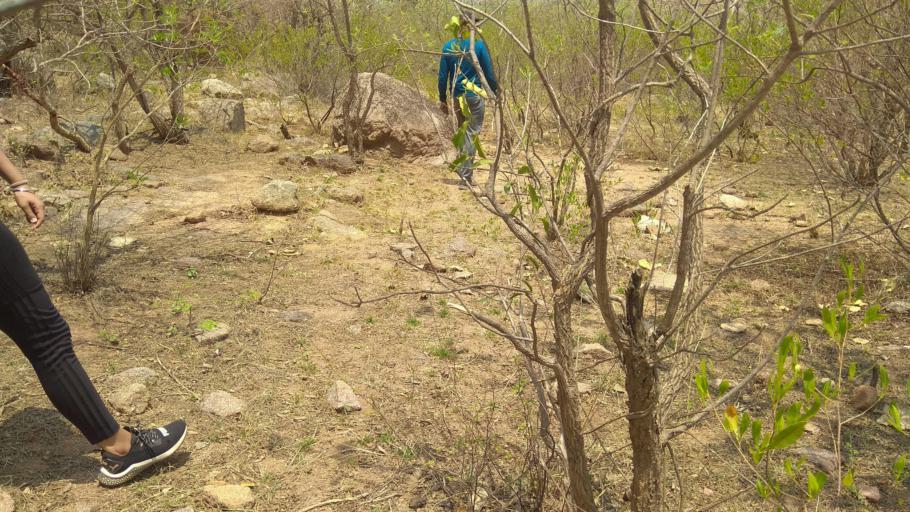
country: IN
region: Telangana
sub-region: Mahbubnagar
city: Farrukhnagar
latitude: 16.8853
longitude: 78.4988
